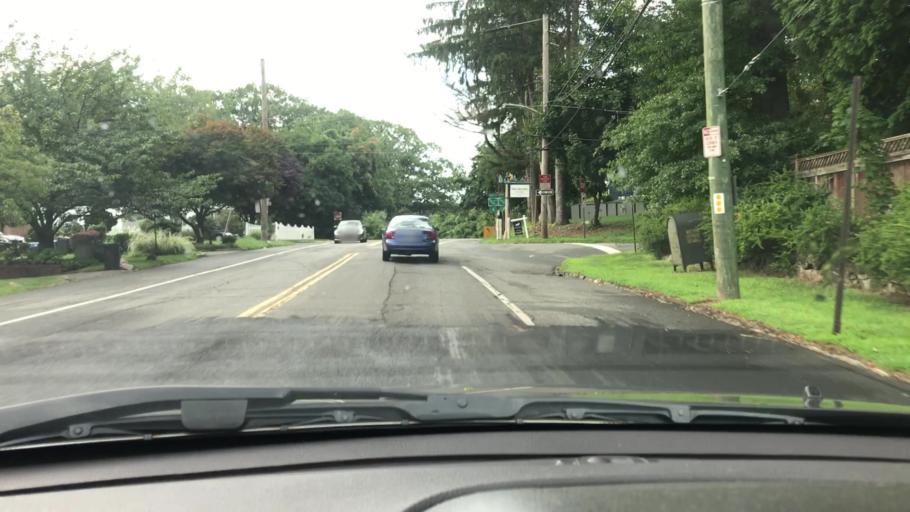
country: US
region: New York
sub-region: Westchester County
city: Tuckahoe
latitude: 40.9427
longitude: -73.8001
